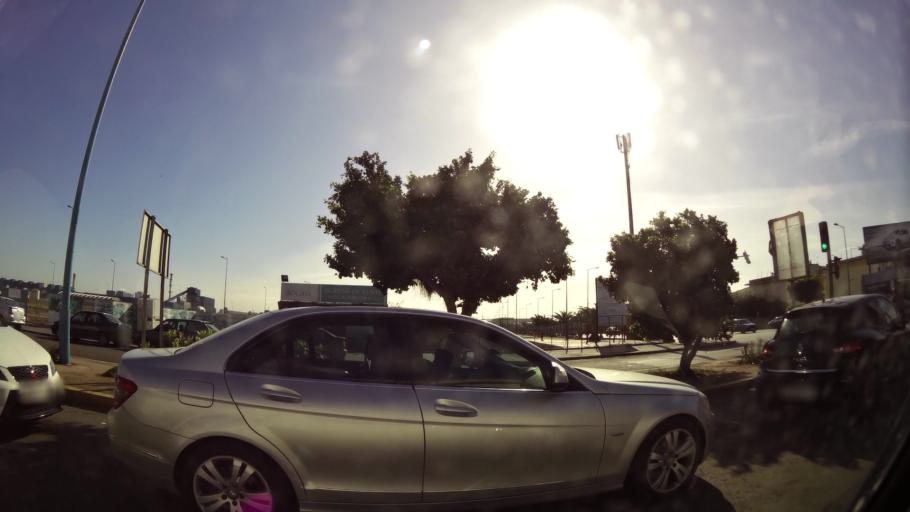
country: MA
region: Grand Casablanca
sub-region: Casablanca
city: Casablanca
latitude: 33.5986
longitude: -7.5773
